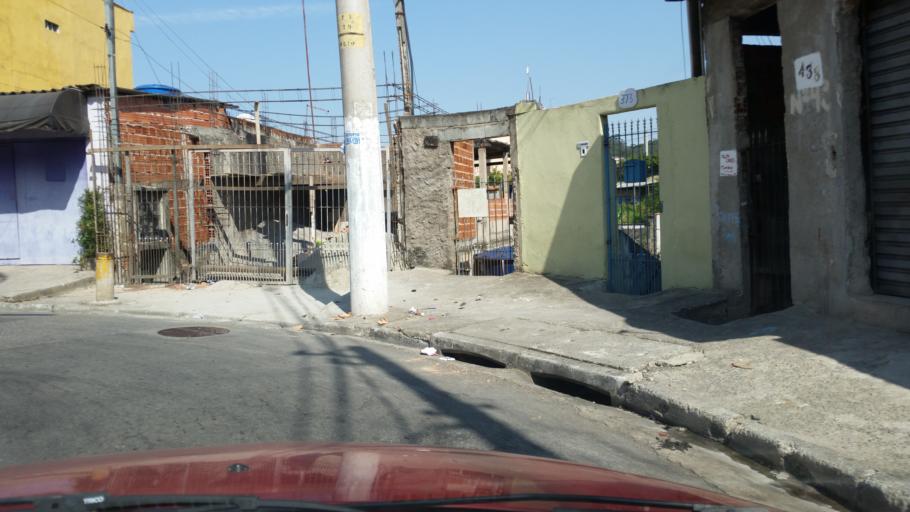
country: BR
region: Sao Paulo
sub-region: Ferraz De Vasconcelos
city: Ferraz de Vasconcelos
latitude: -23.5639
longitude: -46.4226
